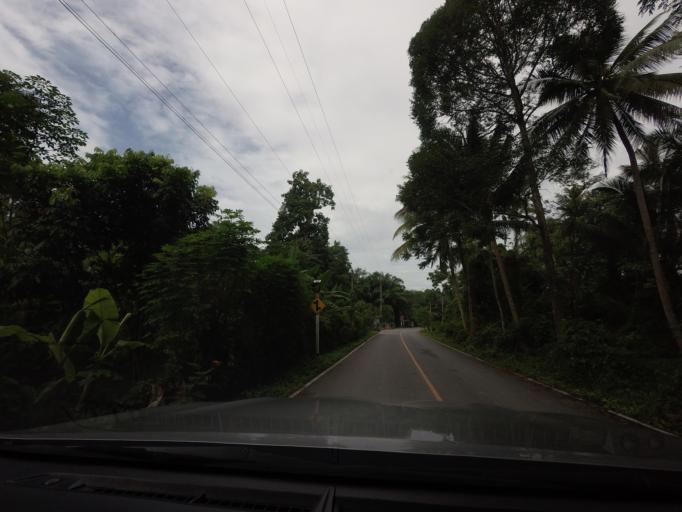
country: TH
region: Nakhon Si Thammarat
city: Phra Phrom
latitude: 8.2833
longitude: 99.9306
